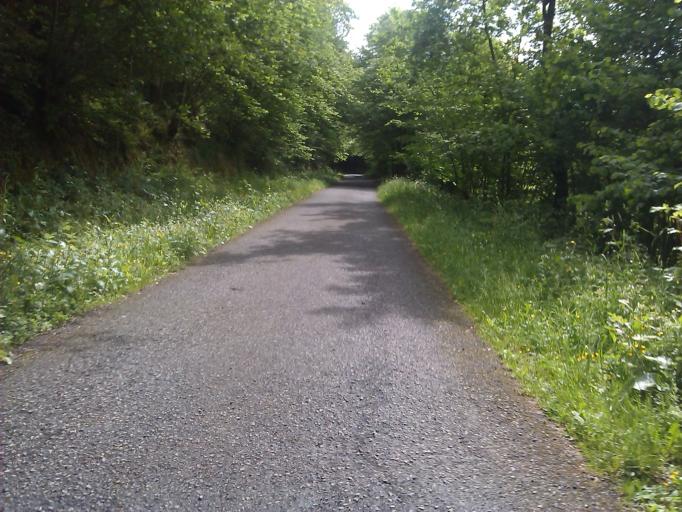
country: ES
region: Navarre
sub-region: Provincia de Navarra
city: Areso
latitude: 43.1048
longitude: -1.9384
